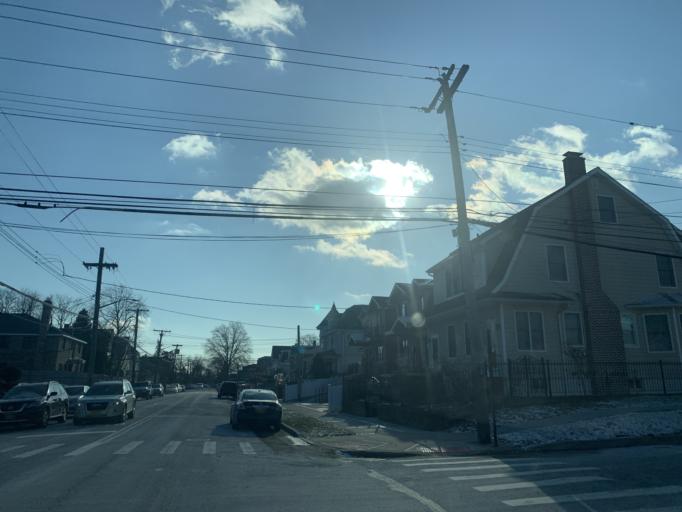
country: US
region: New York
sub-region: Nassau County
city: East Atlantic Beach
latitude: 40.7840
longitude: -73.8168
